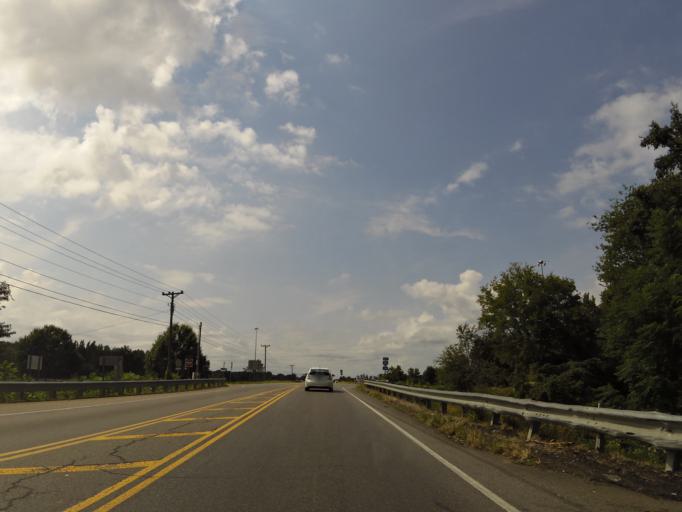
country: US
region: Tennessee
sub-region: Humphreys County
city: Waverly
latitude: 35.8812
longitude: -87.8009
